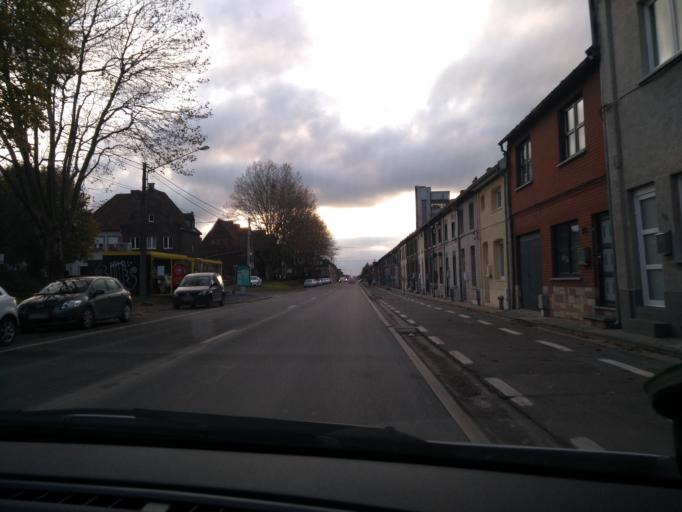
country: BE
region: Wallonia
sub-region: Province du Hainaut
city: Binche
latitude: 50.4310
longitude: 4.1912
